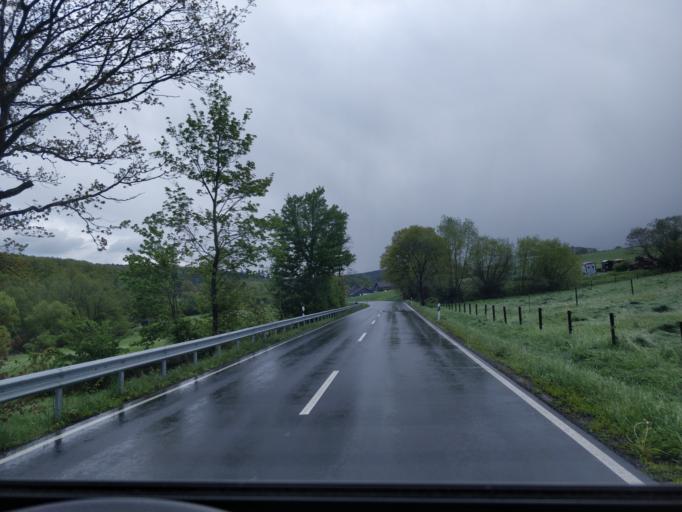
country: DE
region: North Rhine-Westphalia
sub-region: Regierungsbezirk Koln
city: Rheinbach
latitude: 50.5929
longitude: 6.8975
